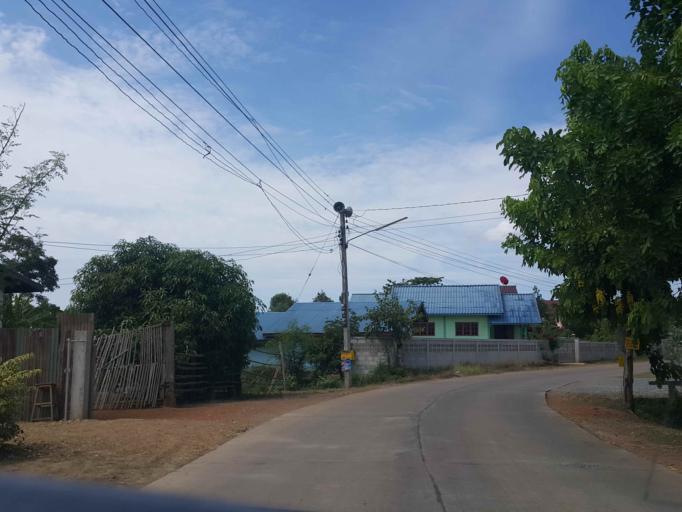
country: TH
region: Sukhothai
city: Thung Saliam
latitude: 17.3312
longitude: 99.5653
